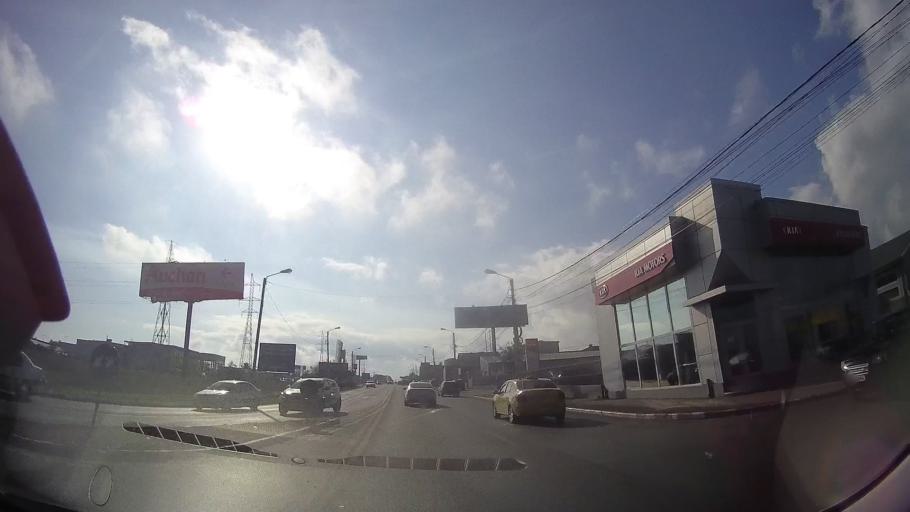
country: RO
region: Constanta
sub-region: Municipiul Constanta
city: Constanta
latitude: 44.1379
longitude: 28.6207
